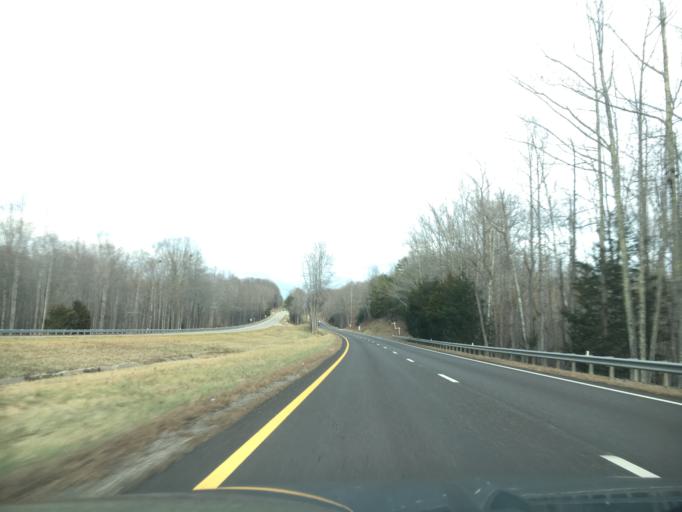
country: US
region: Virginia
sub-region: Lunenburg County
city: Victoria
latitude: 37.1240
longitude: -78.3285
